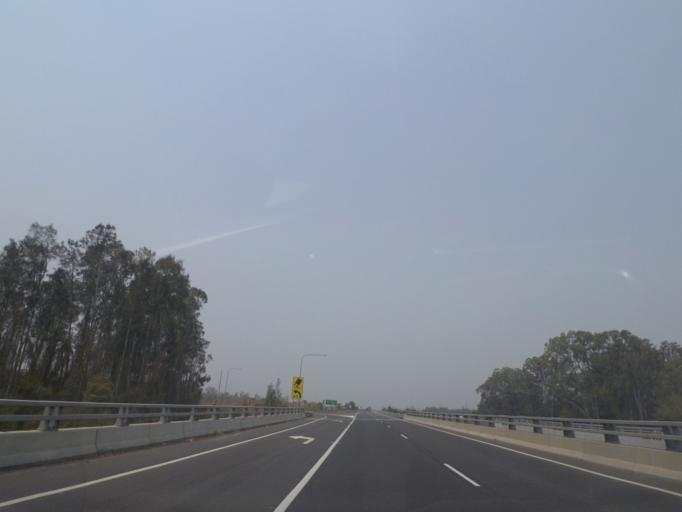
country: AU
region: New South Wales
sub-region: Ballina
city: Ballina
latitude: -28.8661
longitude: 153.4978
